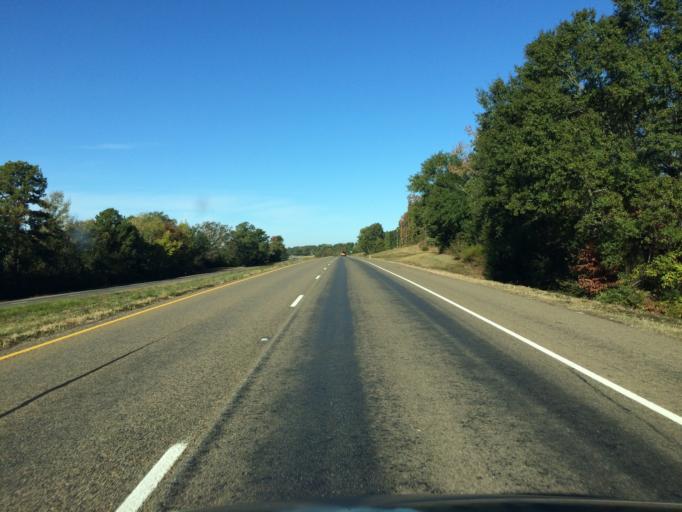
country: US
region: Texas
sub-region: Wood County
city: Hawkins
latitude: 32.5913
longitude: -95.2244
